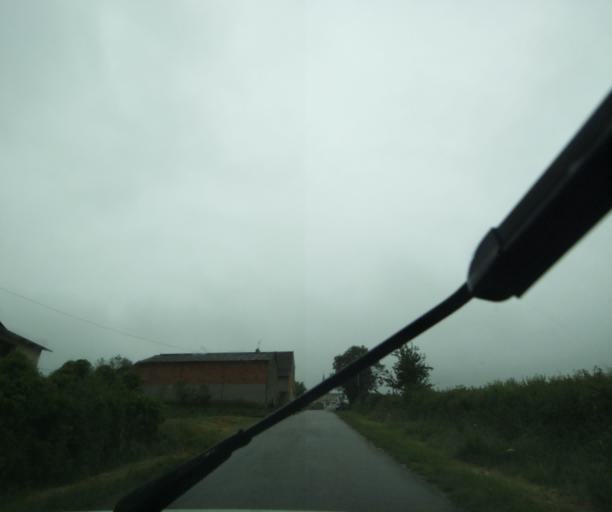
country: FR
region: Bourgogne
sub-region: Departement de Saone-et-Loire
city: Charolles
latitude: 46.4058
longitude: 4.2537
